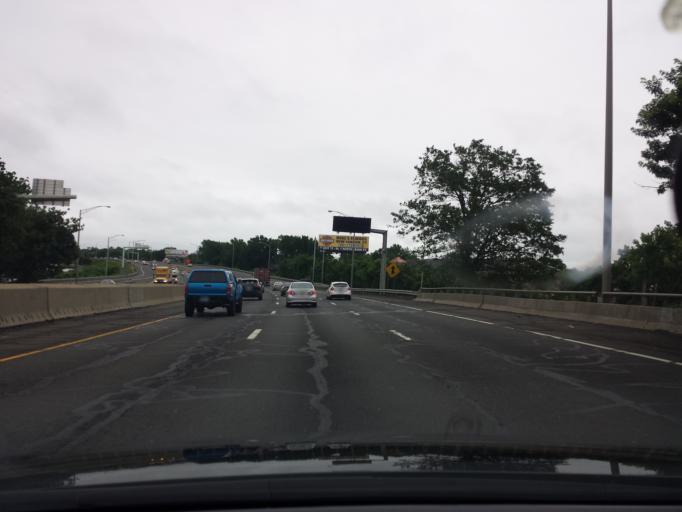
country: US
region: Connecticut
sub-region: Fairfield County
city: Stratford
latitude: 41.1837
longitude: -73.1400
